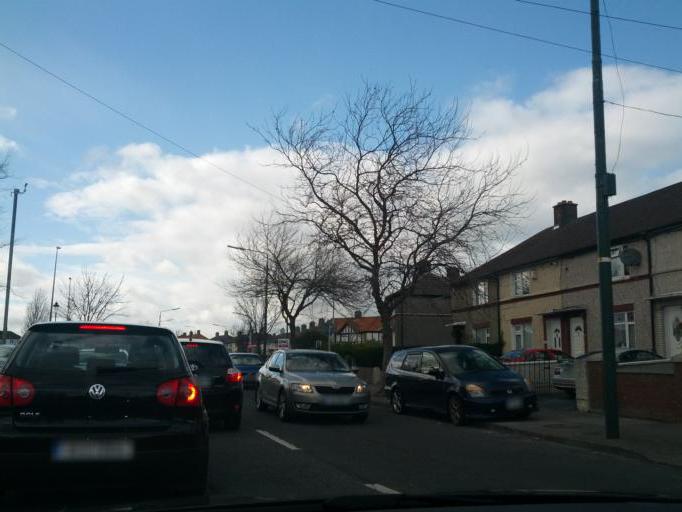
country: IE
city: Donnycarney
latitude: 53.3750
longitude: -6.2177
